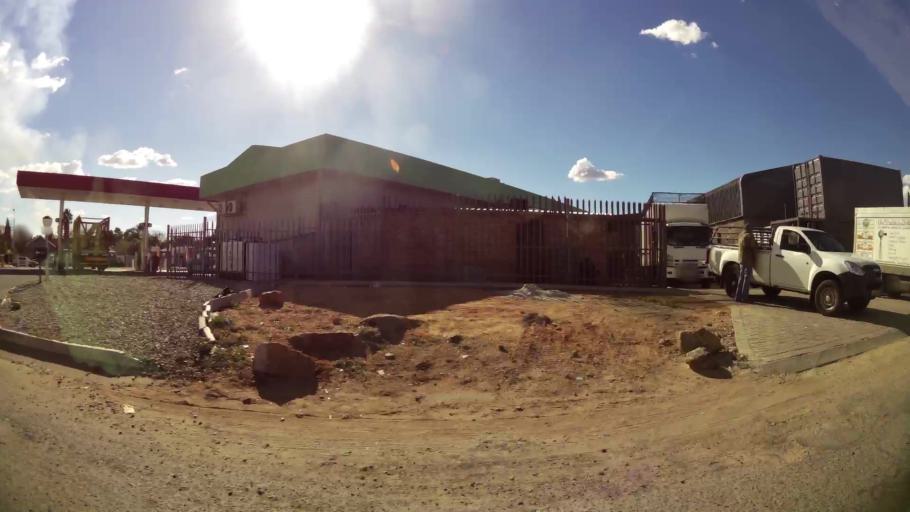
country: ZA
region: North-West
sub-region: Dr Kenneth Kaunda District Municipality
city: Klerksdorp
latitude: -26.8380
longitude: 26.6554
